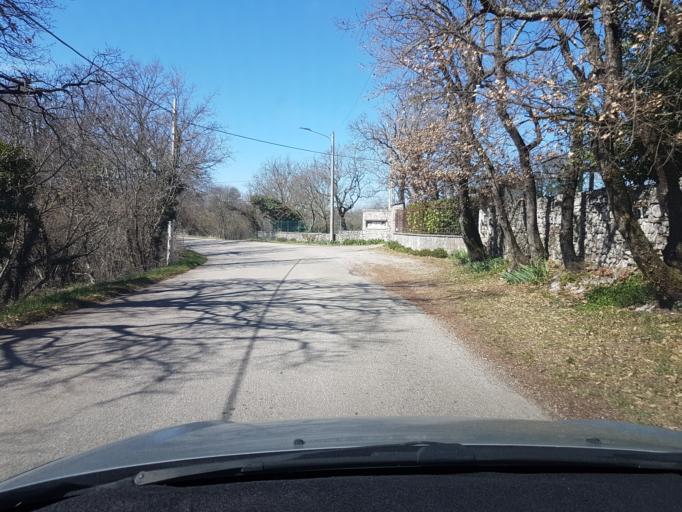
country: IT
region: Friuli Venezia Giulia
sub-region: Provincia di Trieste
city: Sgonico
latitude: 45.7478
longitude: 13.7247
